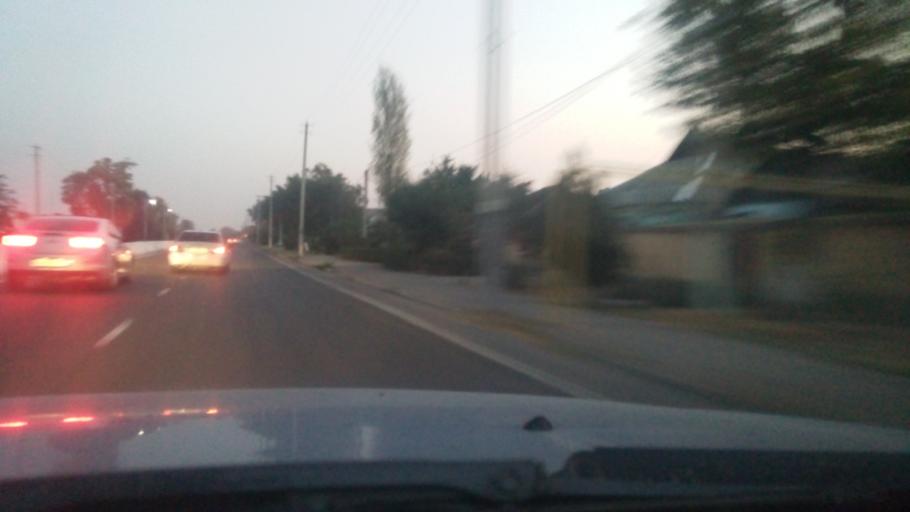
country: UZ
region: Sirdaryo
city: Sirdaryo
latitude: 40.8241
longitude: 68.6778
